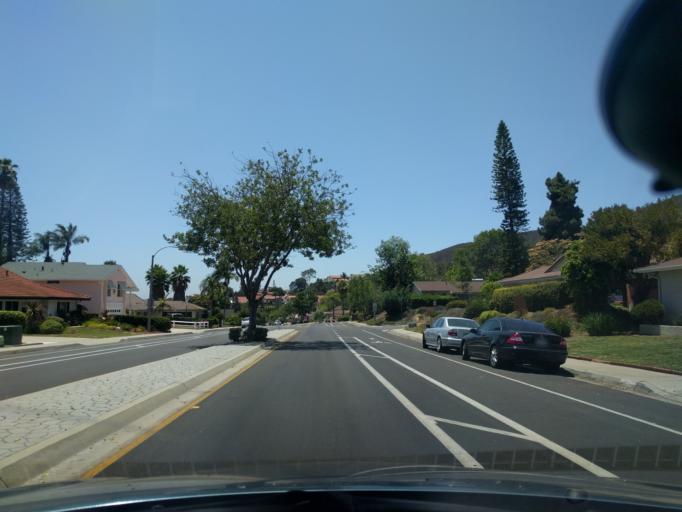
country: US
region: California
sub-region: San Diego County
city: Poway
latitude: 32.9829
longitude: -117.0926
